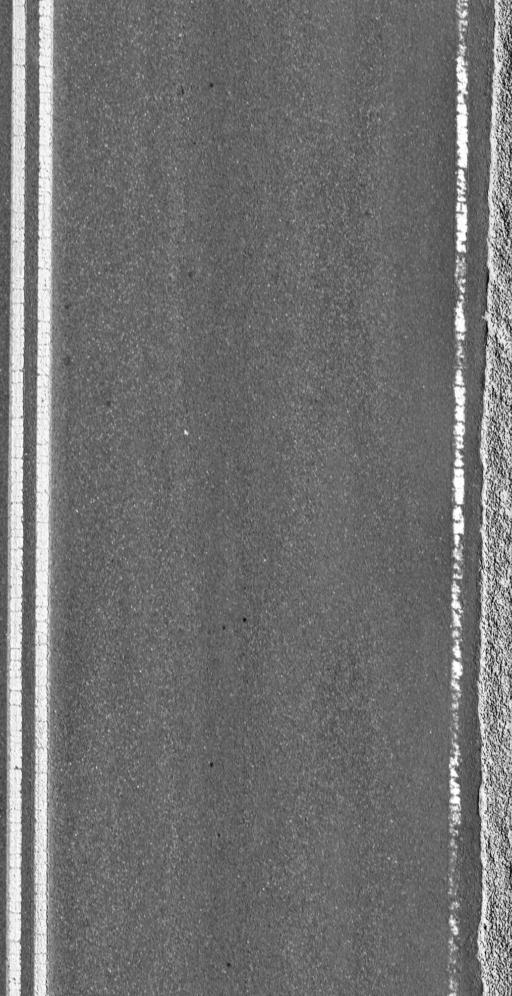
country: US
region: Vermont
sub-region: Windsor County
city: Wilder
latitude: 43.6811
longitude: -72.3224
